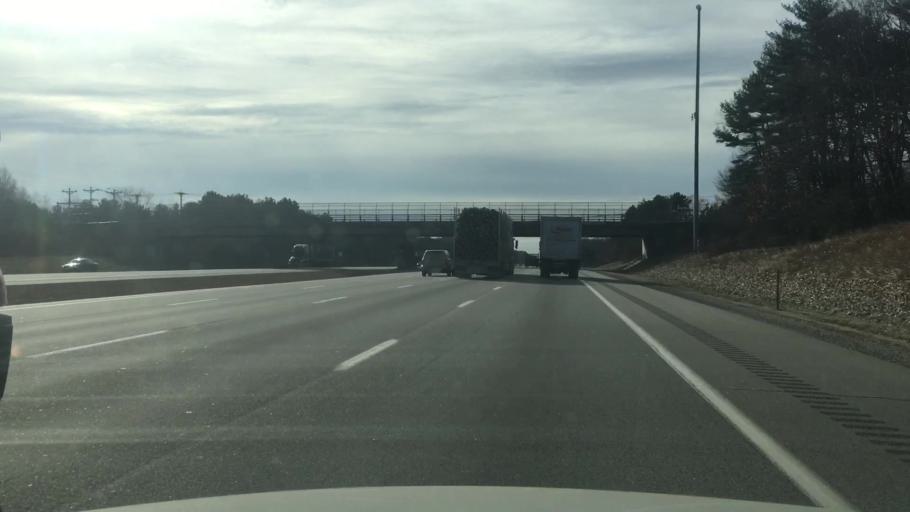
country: US
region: New Hampshire
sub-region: Rockingham County
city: Greenland
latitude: 43.0217
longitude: -70.8299
